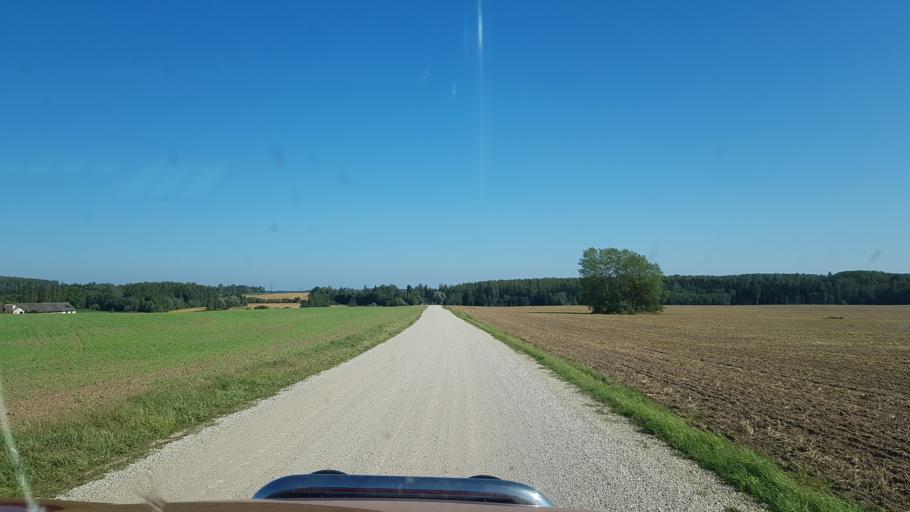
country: EE
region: Tartu
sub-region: UElenurme vald
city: Ulenurme
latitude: 58.2531
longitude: 26.8826
